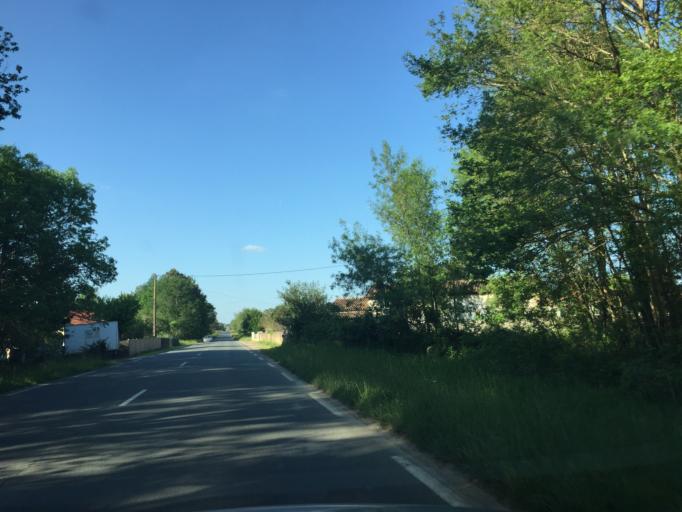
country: FR
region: Aquitaine
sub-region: Departement de la Dordogne
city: La Roche-Chalais
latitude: 45.1675
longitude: 0.0127
